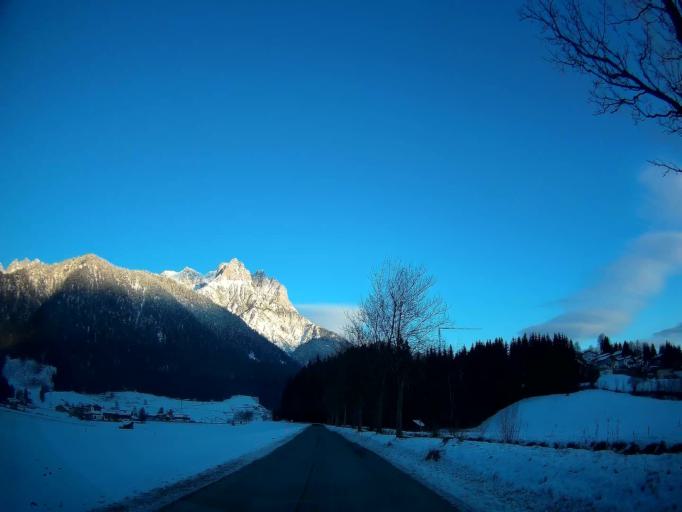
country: AT
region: Salzburg
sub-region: Politischer Bezirk Zell am See
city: Saalfelden am Steinernen Meer
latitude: 47.4516
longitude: 12.8249
